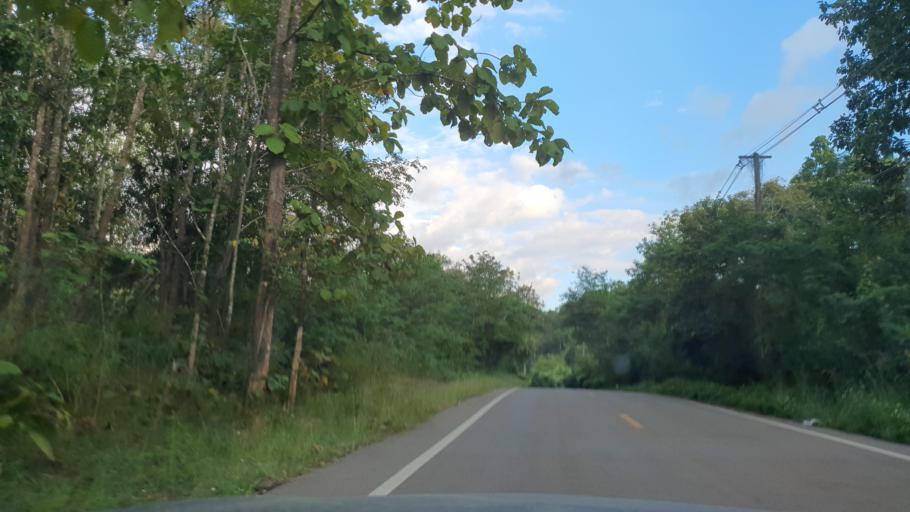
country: TH
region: Chiang Mai
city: Mae On
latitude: 18.8542
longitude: 99.2535
